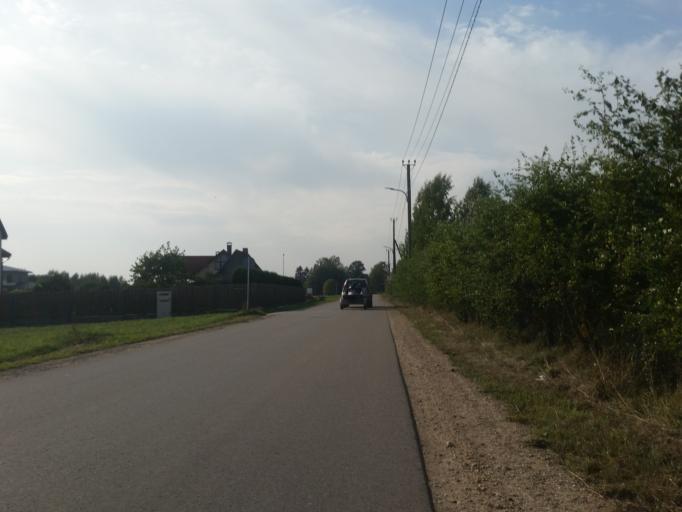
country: LV
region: Ikskile
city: Ikskile
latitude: 56.8188
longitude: 24.5140
